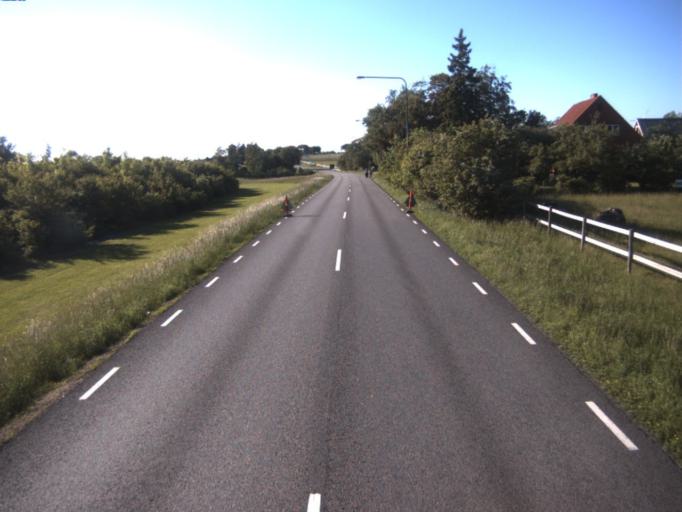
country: SE
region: Skane
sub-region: Helsingborg
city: Rydeback
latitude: 55.9743
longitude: 12.7772
